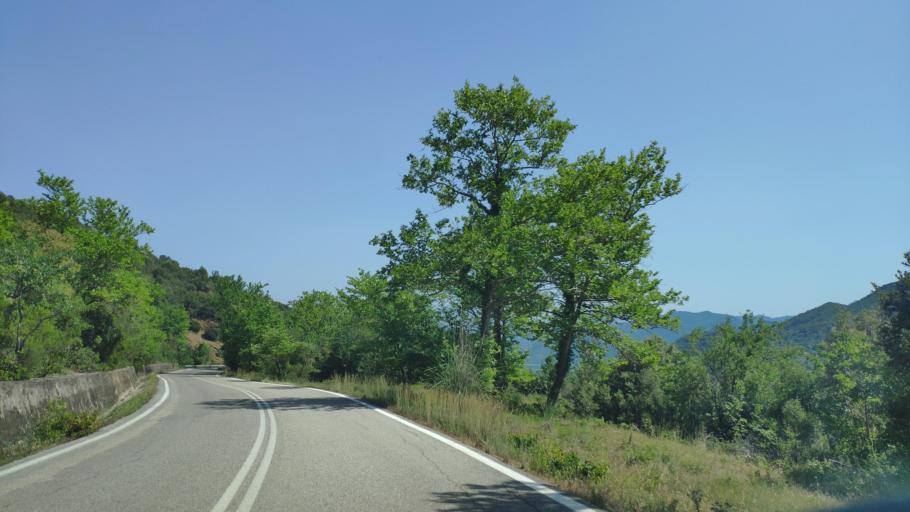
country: GR
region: West Greece
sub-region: Nomos Aitolias kai Akarnanias
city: Lepenou
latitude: 38.7978
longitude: 21.3325
